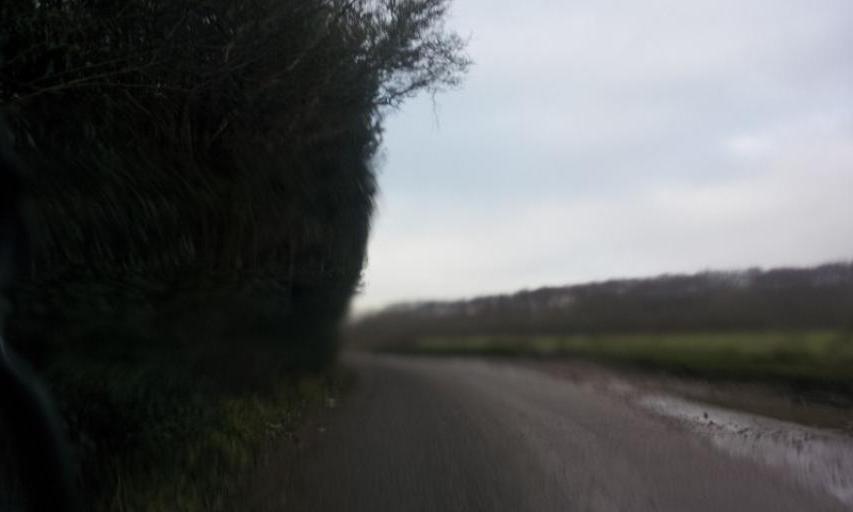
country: GB
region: England
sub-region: Kent
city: Boxley
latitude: 51.3232
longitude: 0.5542
